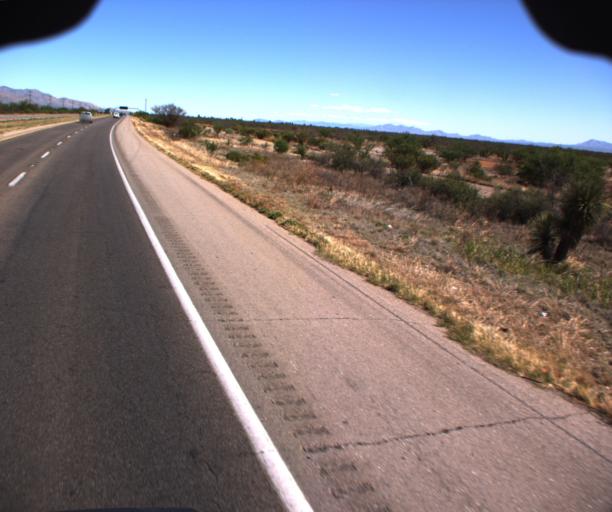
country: US
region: Arizona
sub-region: Cochise County
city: Huachuca City
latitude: 31.6641
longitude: -110.3501
